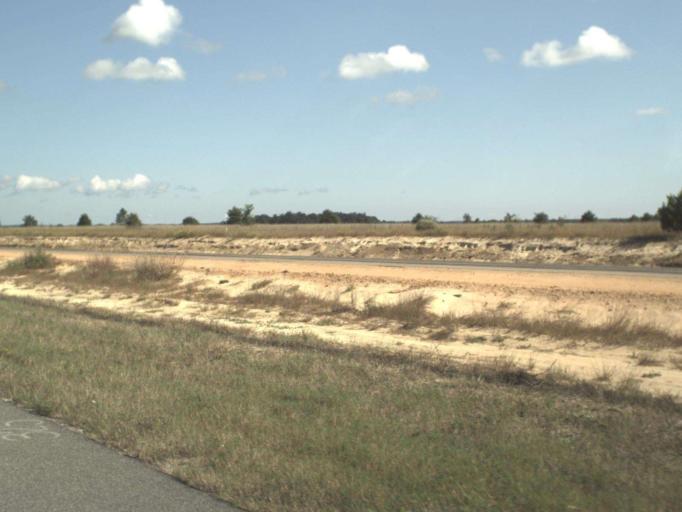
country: US
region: Florida
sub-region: Walton County
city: Freeport
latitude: 30.5442
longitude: -86.1070
